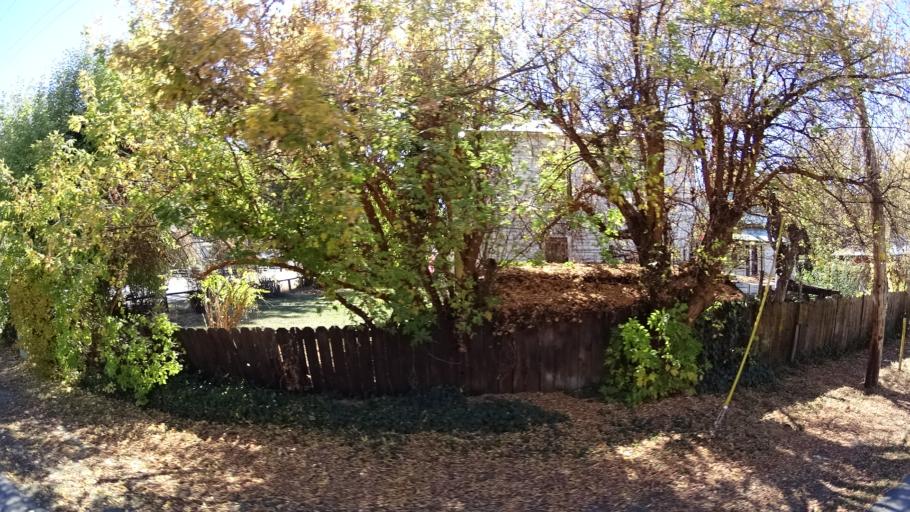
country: US
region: California
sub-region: Siskiyou County
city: Yreka
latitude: 41.6052
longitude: -122.8435
